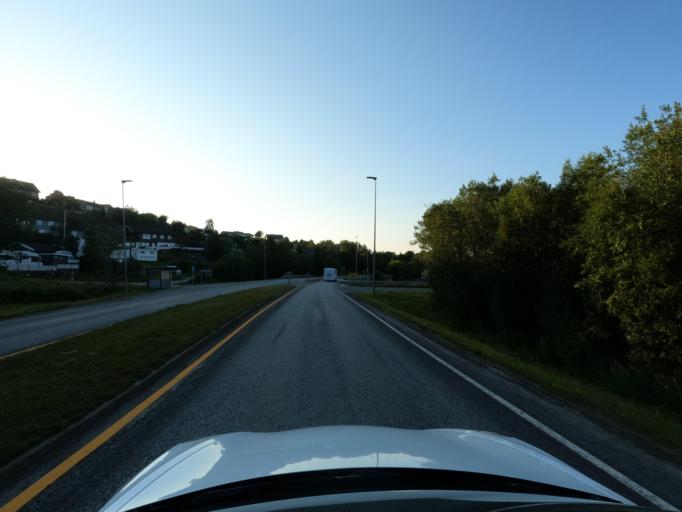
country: NO
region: Troms
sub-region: Harstad
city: Harstad
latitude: 68.7538
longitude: 16.5666
